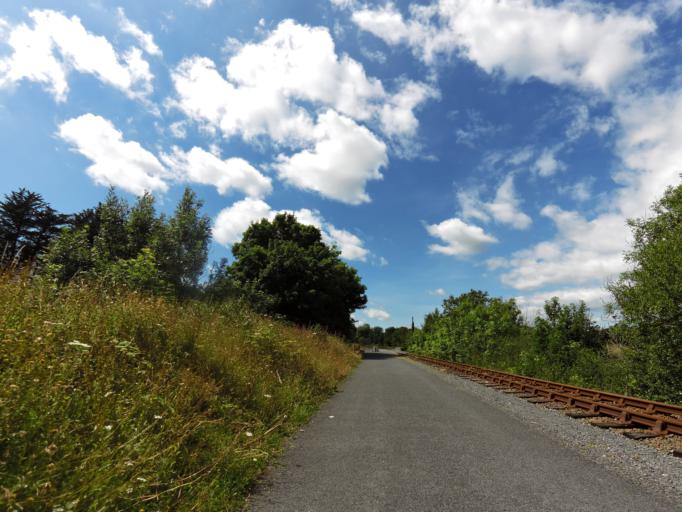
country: IE
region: Leinster
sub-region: Kilkenny
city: Mooncoin
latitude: 52.2473
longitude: -7.2375
